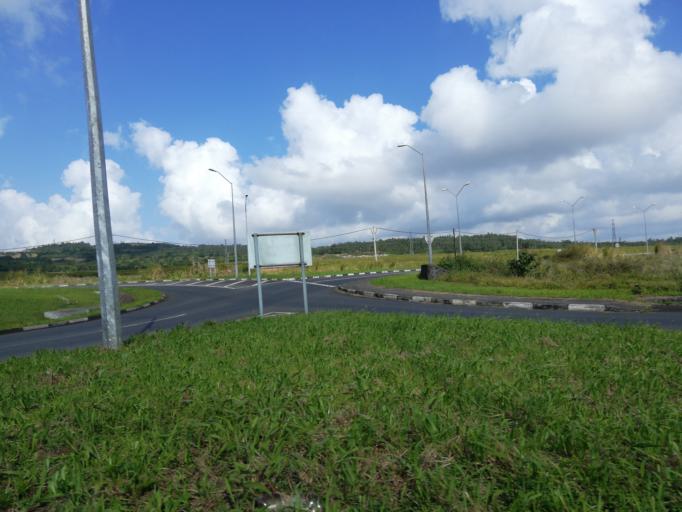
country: MU
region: Pamplemousses
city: Creve Coeur
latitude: -20.2011
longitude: 57.5715
